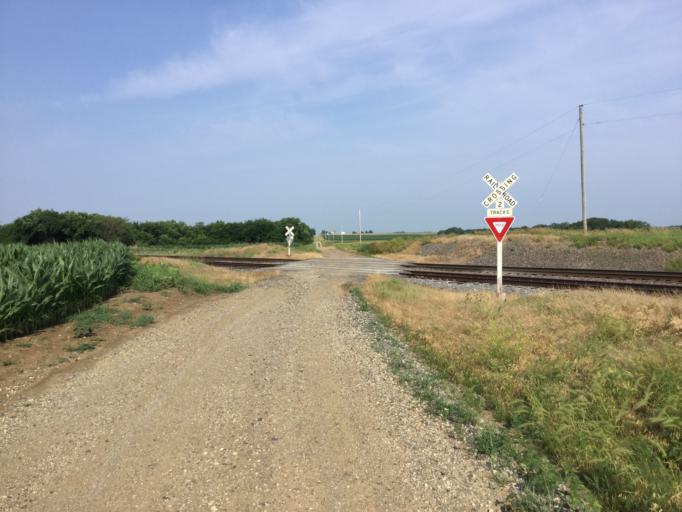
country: US
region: Kansas
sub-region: Anderson County
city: Garnett
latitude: 38.1985
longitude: -95.4474
